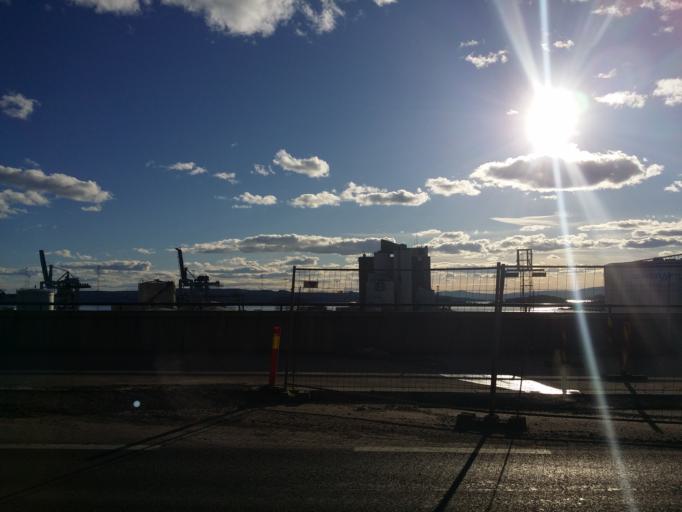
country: NO
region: Oslo
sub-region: Oslo
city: Oslo
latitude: 59.8910
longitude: 10.7615
